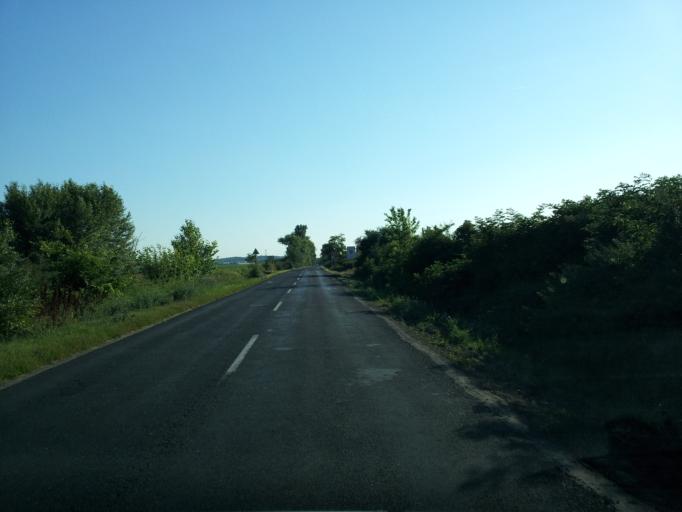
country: HU
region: Fejer
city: Lepseny
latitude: 47.0341
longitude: 18.2264
